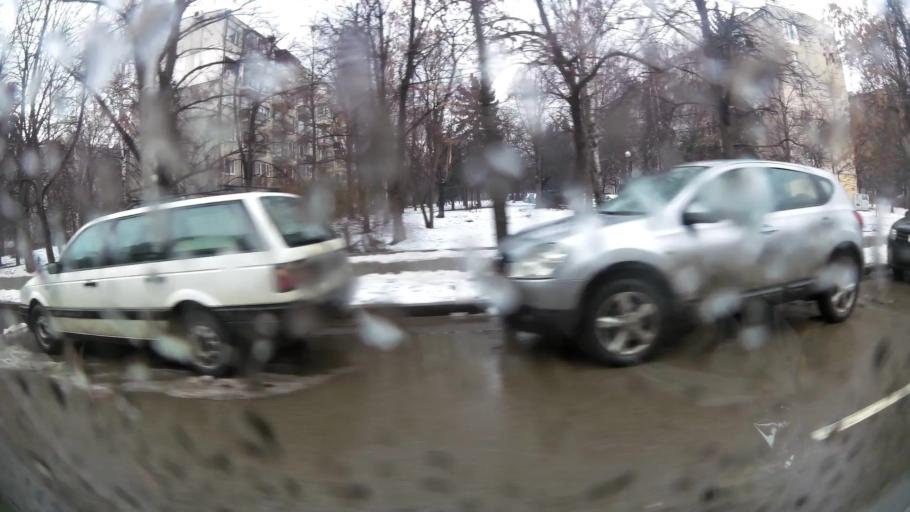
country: BG
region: Sofia-Capital
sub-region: Stolichna Obshtina
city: Sofia
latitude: 42.6626
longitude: 23.2960
